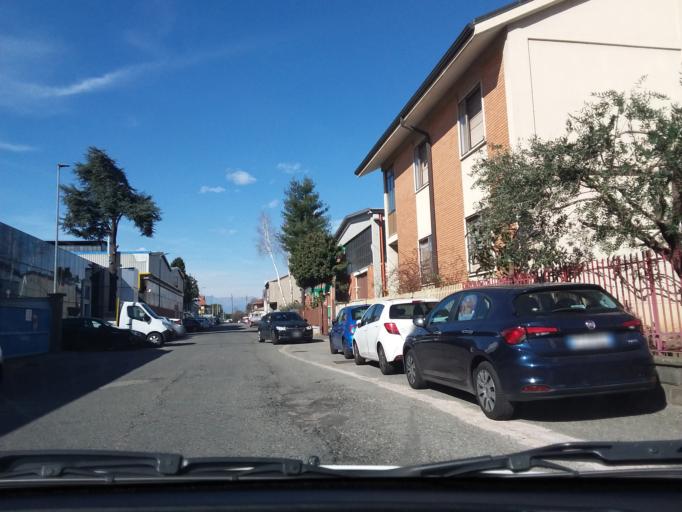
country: IT
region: Piedmont
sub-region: Provincia di Torino
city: Collegno
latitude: 45.0787
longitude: 7.5569
